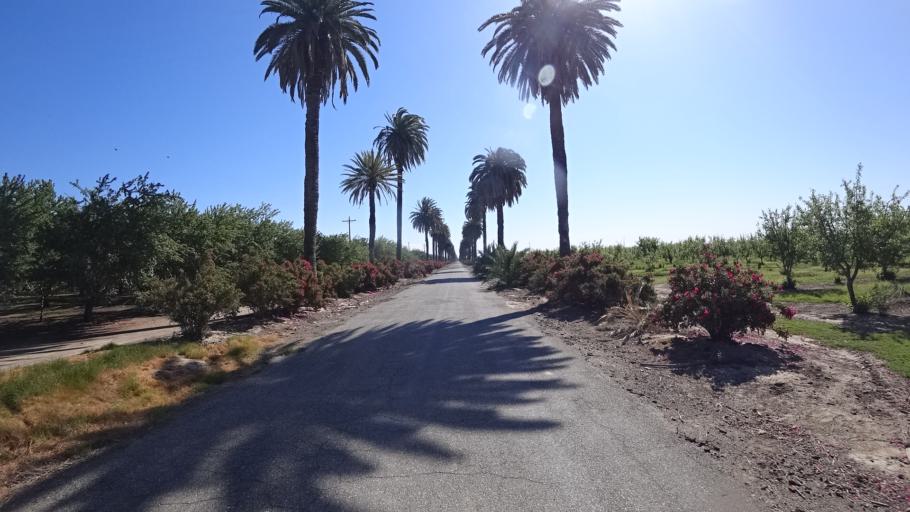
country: US
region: California
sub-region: Glenn County
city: Hamilton City
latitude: 39.7374
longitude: -122.0328
